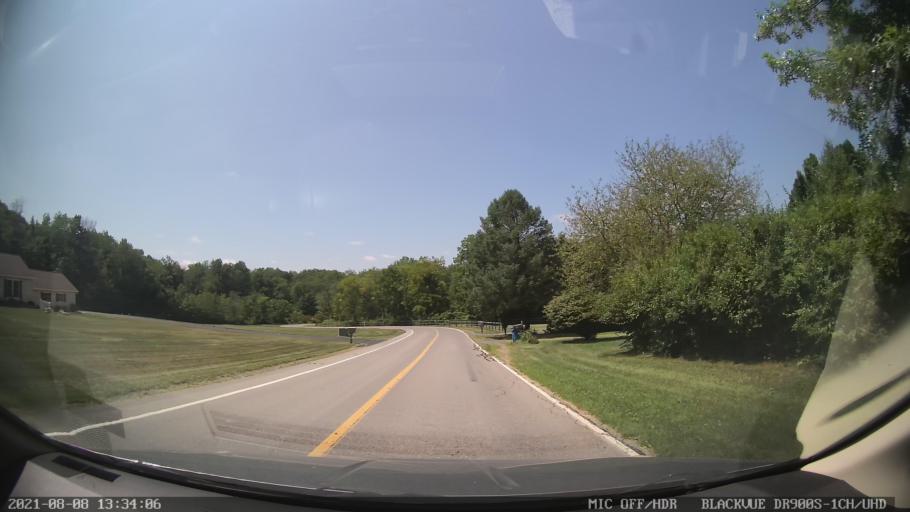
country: US
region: Pennsylvania
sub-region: Berks County
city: Fleetwood
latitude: 40.4478
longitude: -75.7626
